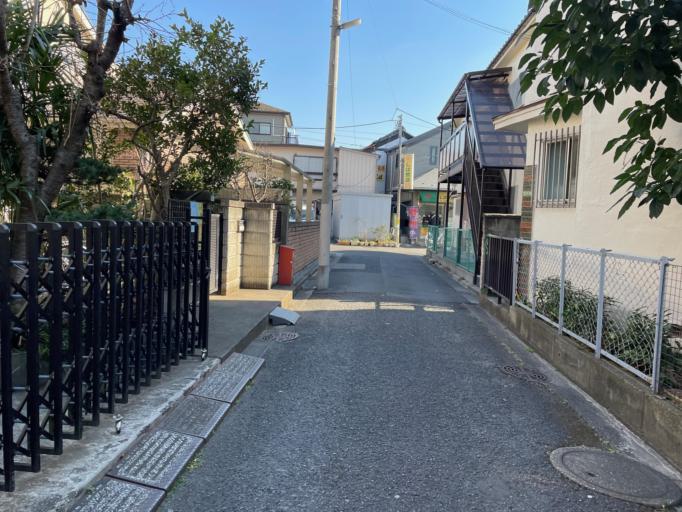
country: JP
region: Saitama
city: Soka
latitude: 35.7765
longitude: 139.7821
